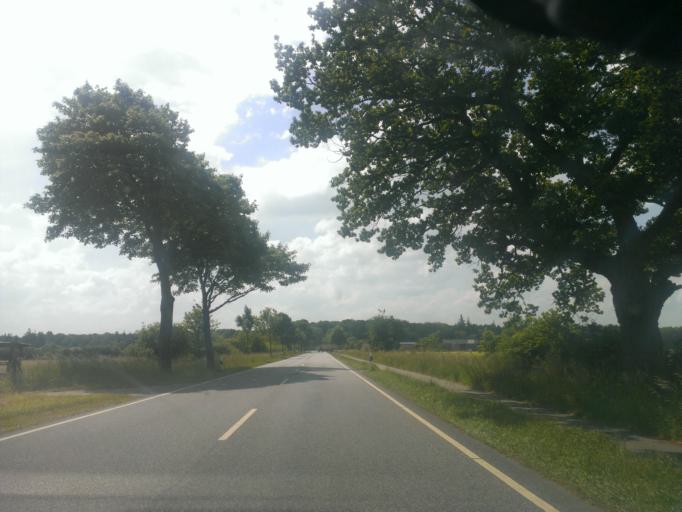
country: DE
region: Schleswig-Holstein
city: Fockbek
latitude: 54.2835
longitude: 9.5770
